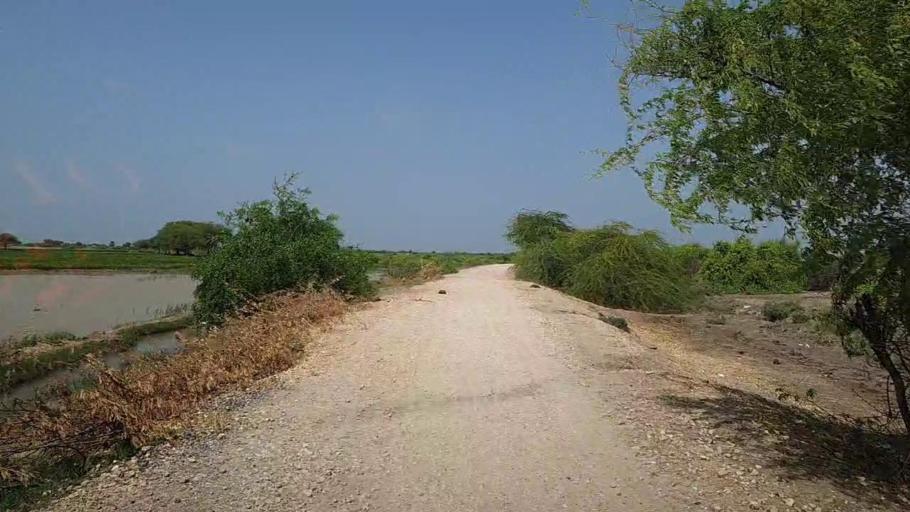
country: PK
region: Sindh
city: Mirpur Batoro
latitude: 24.6483
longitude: 68.4272
